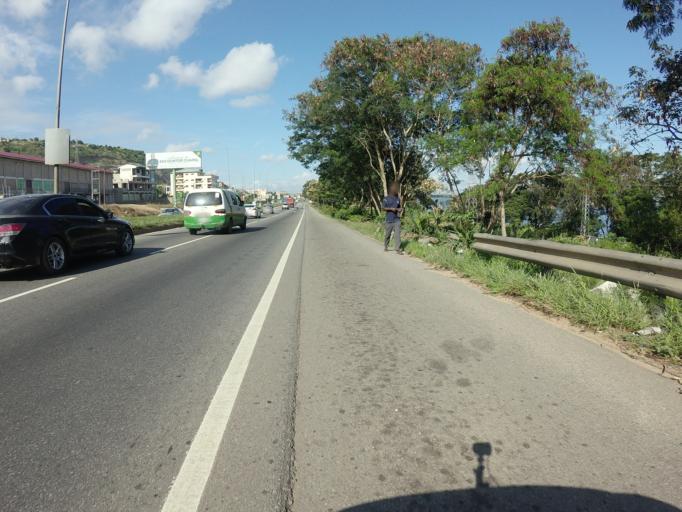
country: GH
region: Central
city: Kasoa
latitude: 5.5524
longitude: -0.3657
